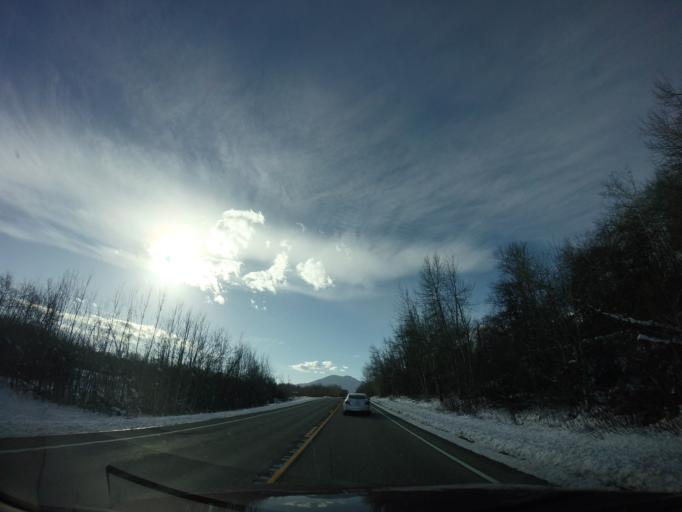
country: US
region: Montana
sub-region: Carbon County
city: Red Lodge
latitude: 45.2271
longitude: -109.2393
